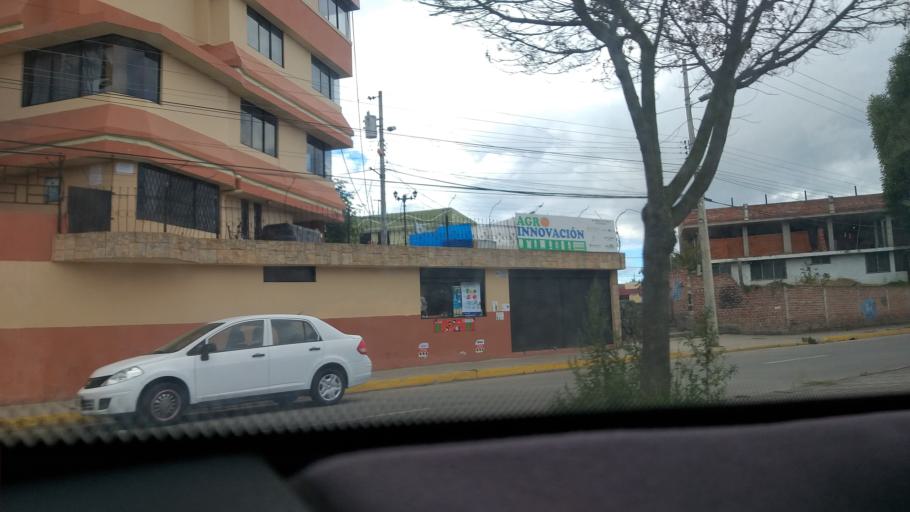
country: EC
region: Chimborazo
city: Riobamba
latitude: -1.6902
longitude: -78.6347
